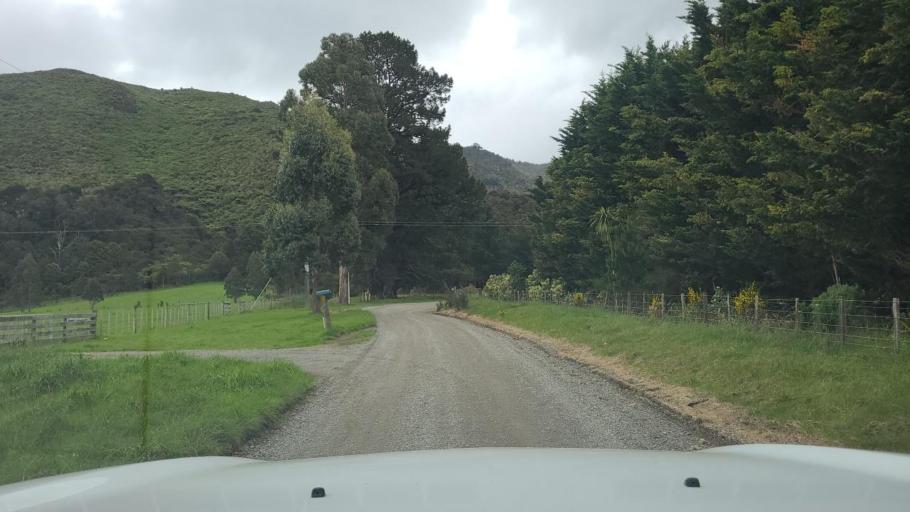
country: NZ
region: Wellington
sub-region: Upper Hutt City
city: Upper Hutt
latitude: -41.0810
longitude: 175.3516
